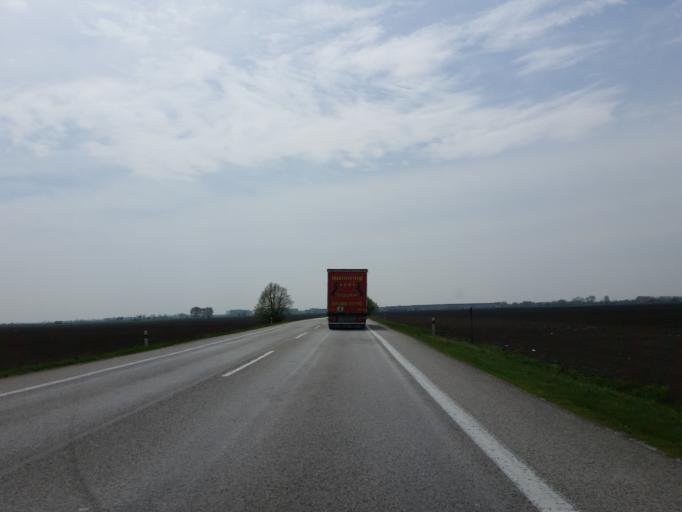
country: SK
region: Trnavsky
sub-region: Okres Galanta
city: Galanta
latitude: 48.2527
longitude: 17.7415
